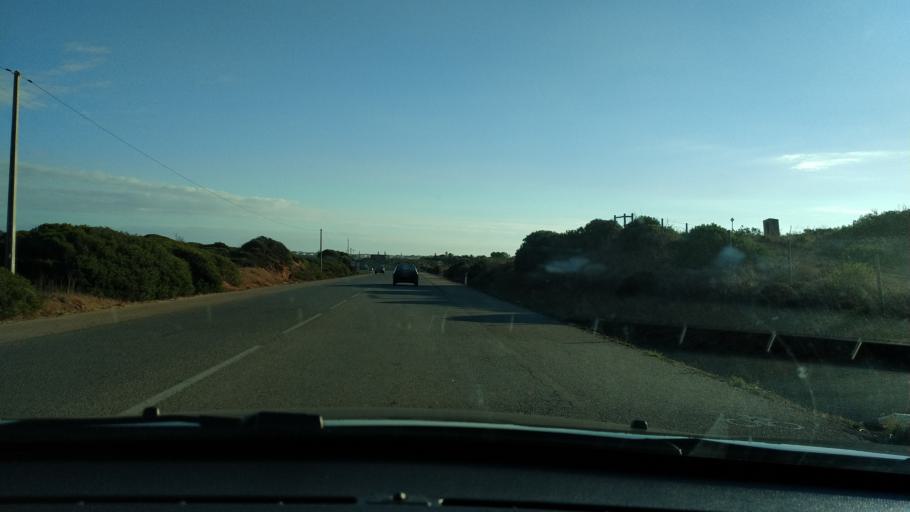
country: PT
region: Faro
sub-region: Vila do Bispo
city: Sagres
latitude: 37.0271
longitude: -8.9372
